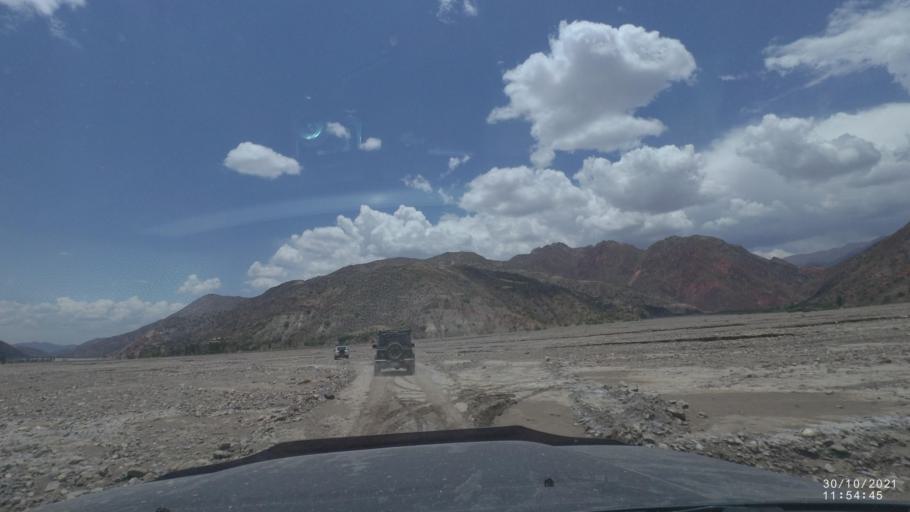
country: BO
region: Cochabamba
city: Colchani
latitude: -17.5192
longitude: -66.6202
